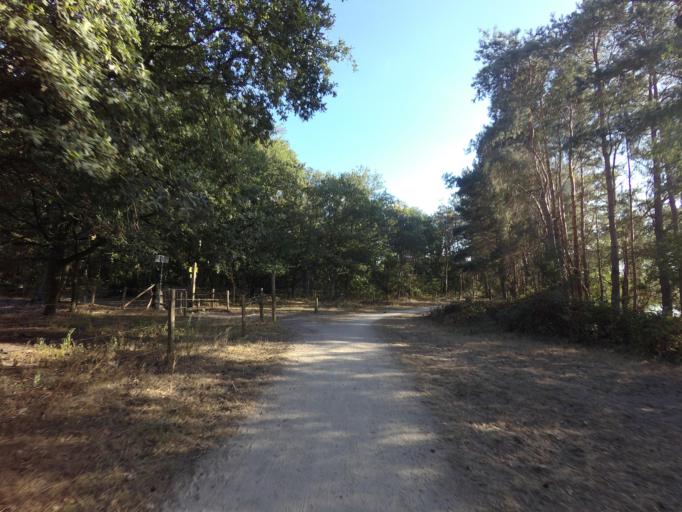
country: NL
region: North Brabant
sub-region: Gemeente Mill en Sint Hubert
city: Wilbertoord
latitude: 51.6944
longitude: 5.7531
